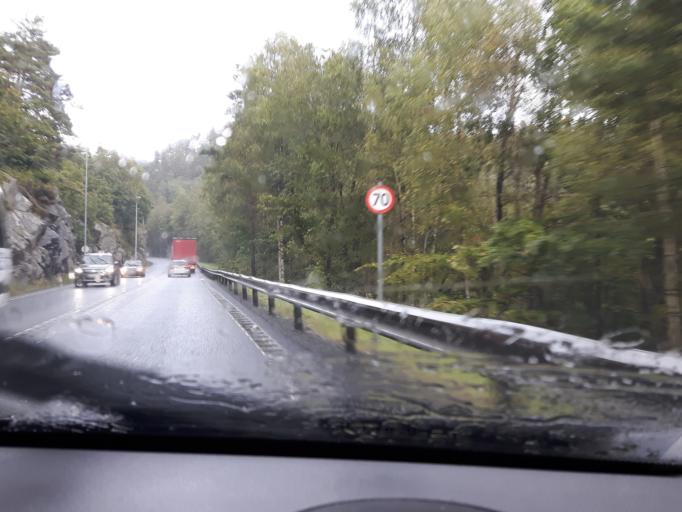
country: NO
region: Vest-Agder
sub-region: Sogne
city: Sogne
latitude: 58.0942
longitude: 7.6918
